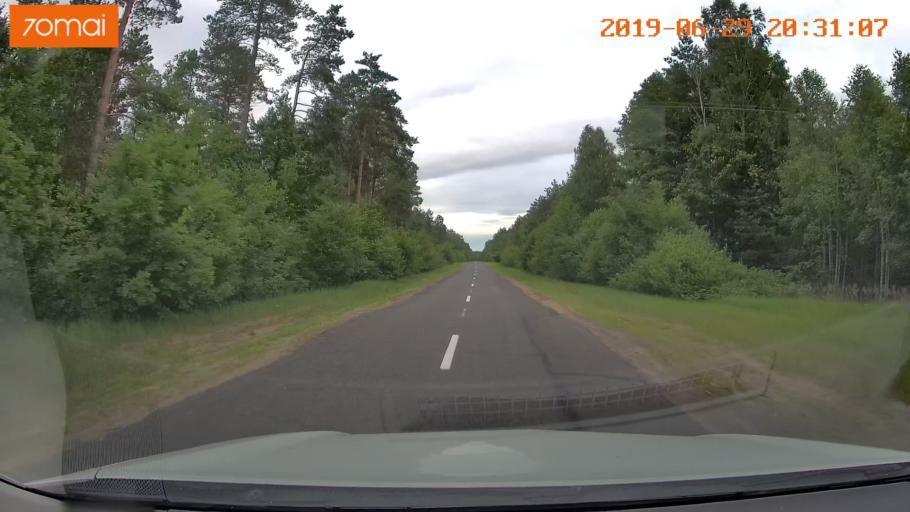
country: BY
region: Brest
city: Hantsavichy
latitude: 52.5113
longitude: 26.3388
